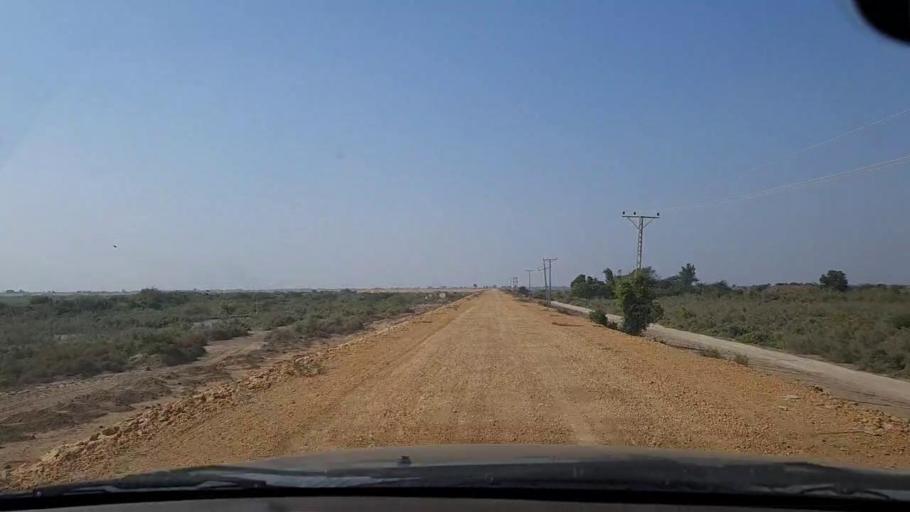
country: PK
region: Sindh
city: Chuhar Jamali
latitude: 24.4622
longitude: 67.8868
